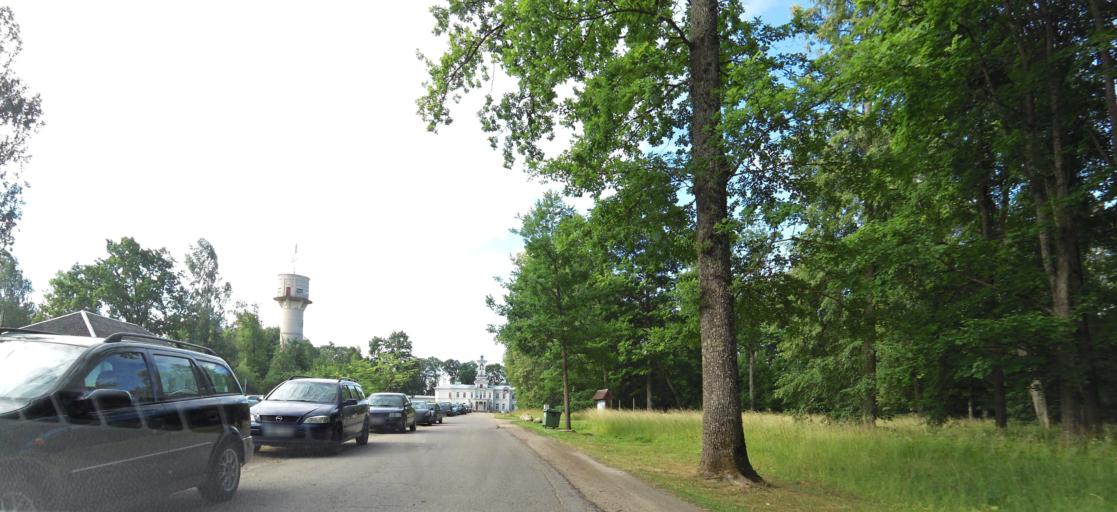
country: LT
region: Panevezys
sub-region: Birzai
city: Birzai
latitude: 56.2217
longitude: 24.7699
